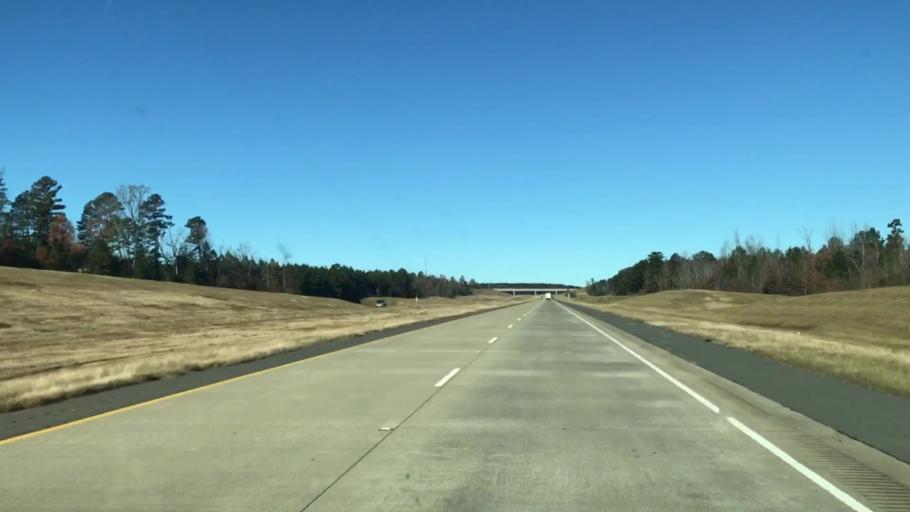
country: US
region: Louisiana
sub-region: Caddo Parish
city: Vivian
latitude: 32.9150
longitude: -93.8764
